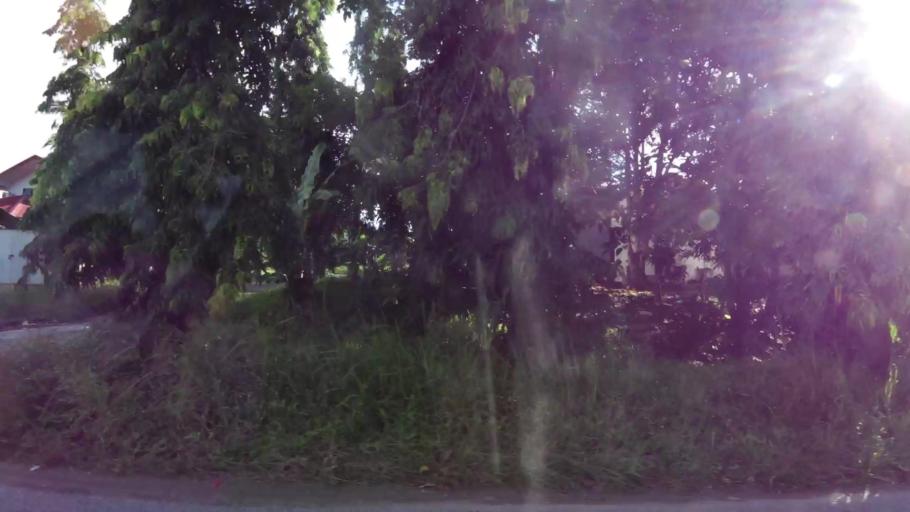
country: BN
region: Brunei and Muara
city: Bandar Seri Begawan
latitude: 4.9887
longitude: 114.9732
